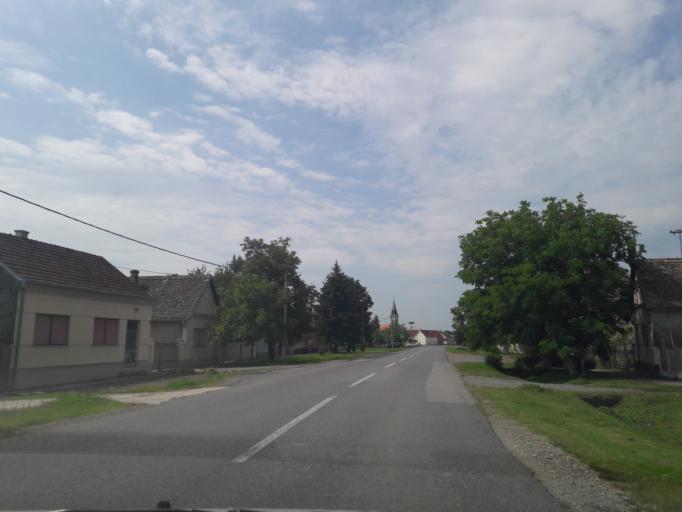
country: HR
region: Osjecko-Baranjska
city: Bizovac
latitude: 45.5124
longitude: 18.4714
